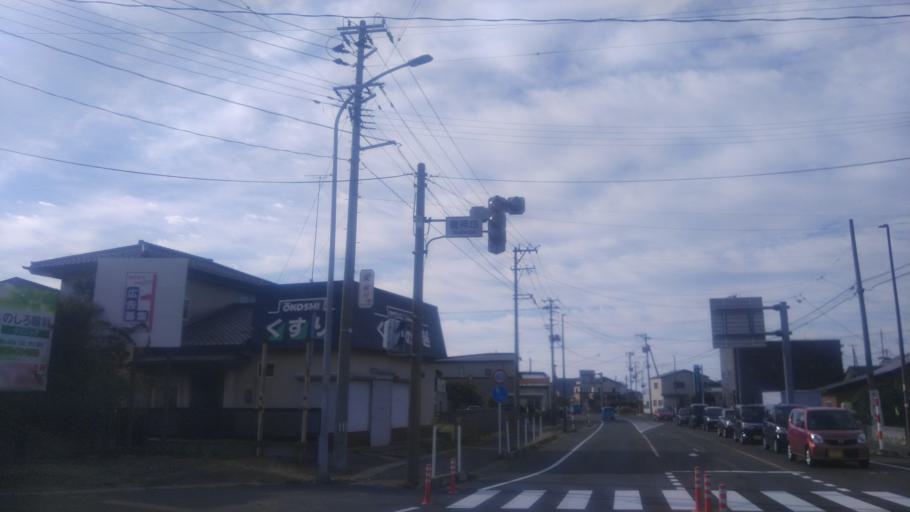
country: JP
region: Akita
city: Noshiromachi
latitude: 40.1912
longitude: 140.0292
